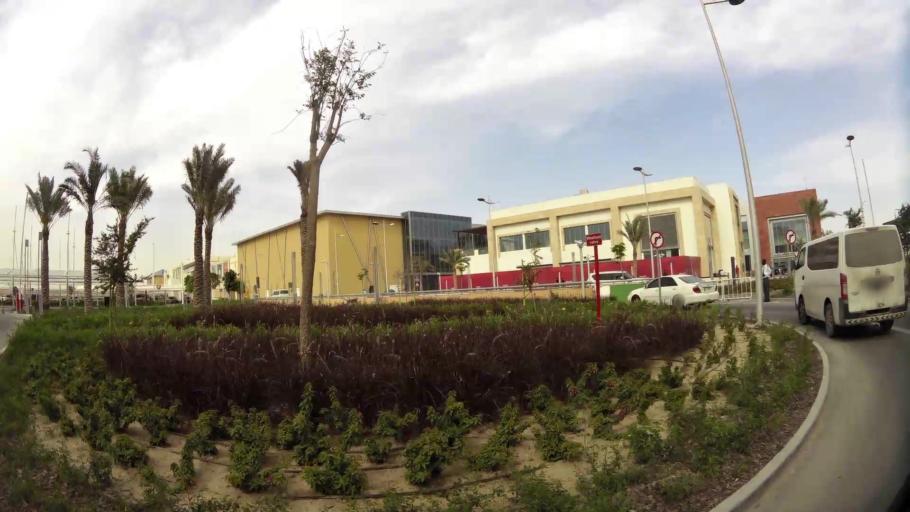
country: QA
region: Baladiyat ar Rayyan
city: Ar Rayyan
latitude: 25.3247
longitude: 51.3480
